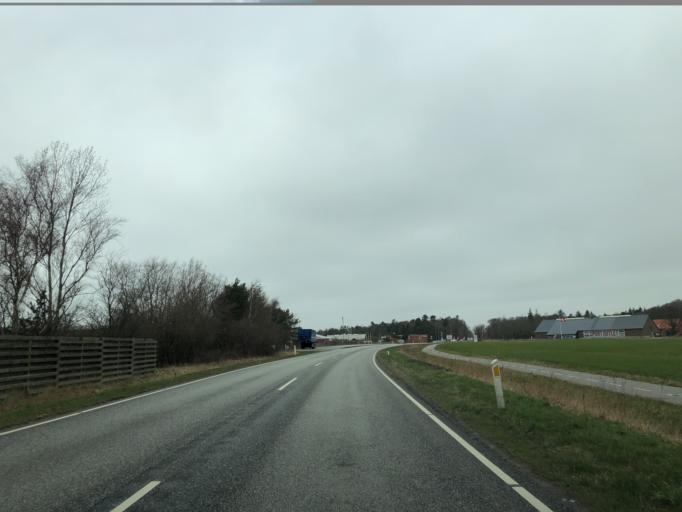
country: DK
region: North Denmark
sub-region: Frederikshavn Kommune
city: Strandby
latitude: 57.4794
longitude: 10.4821
